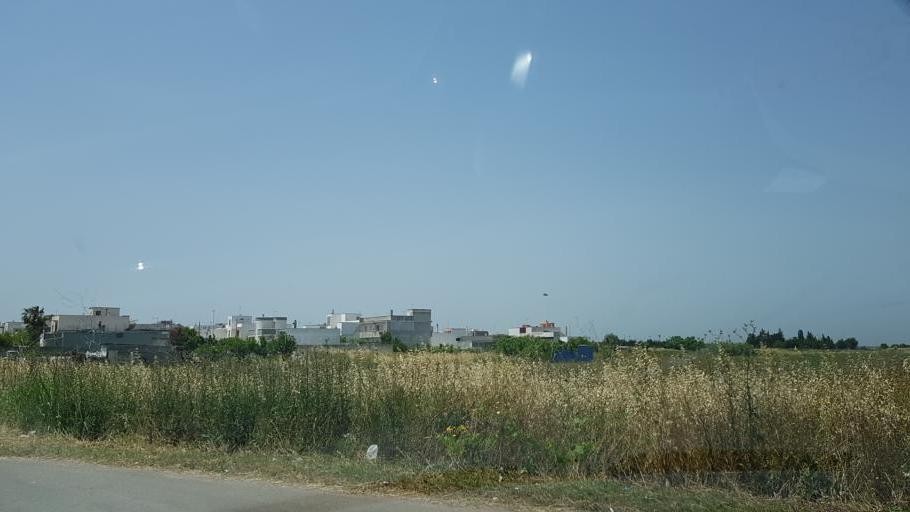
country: IT
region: Apulia
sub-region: Provincia di Brindisi
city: San Pancrazio Salentino
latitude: 40.4237
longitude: 17.8446
